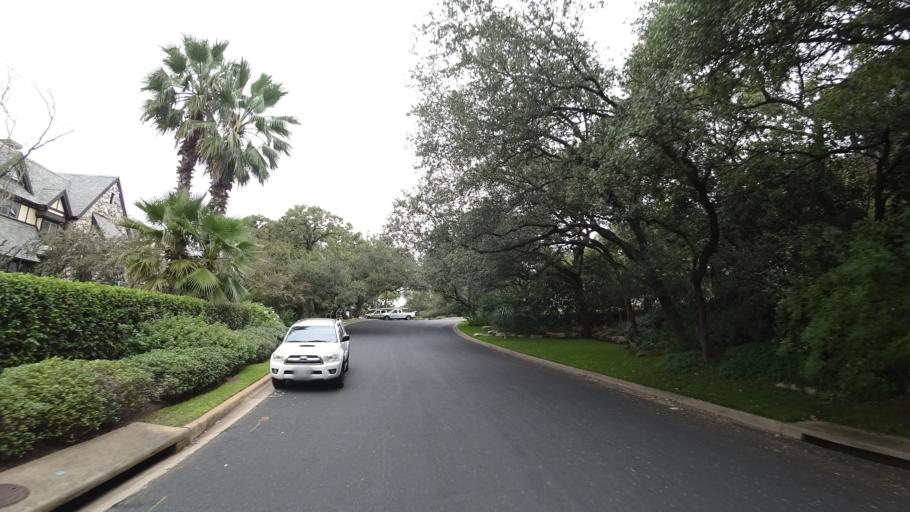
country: US
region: Texas
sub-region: Travis County
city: West Lake Hills
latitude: 30.3068
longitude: -97.7755
